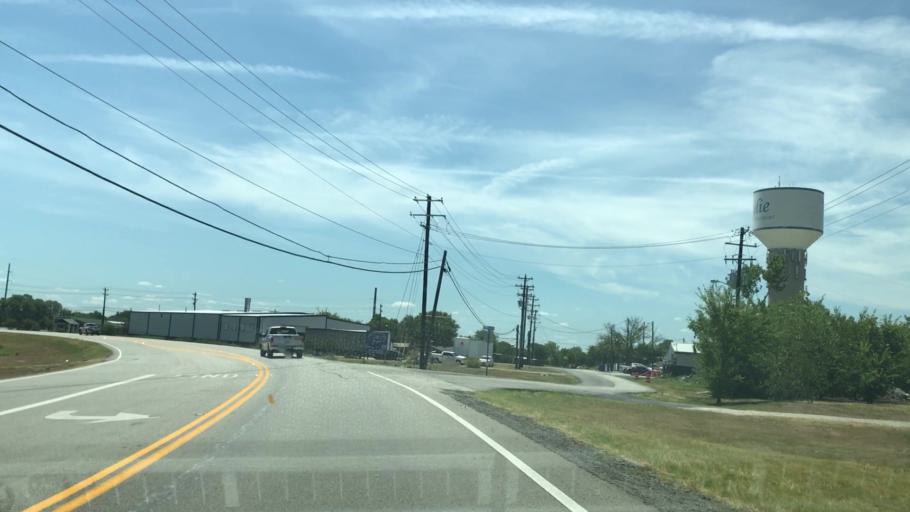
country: US
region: Texas
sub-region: Collin County
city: Saint Paul
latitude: 33.0296
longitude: -96.5471
